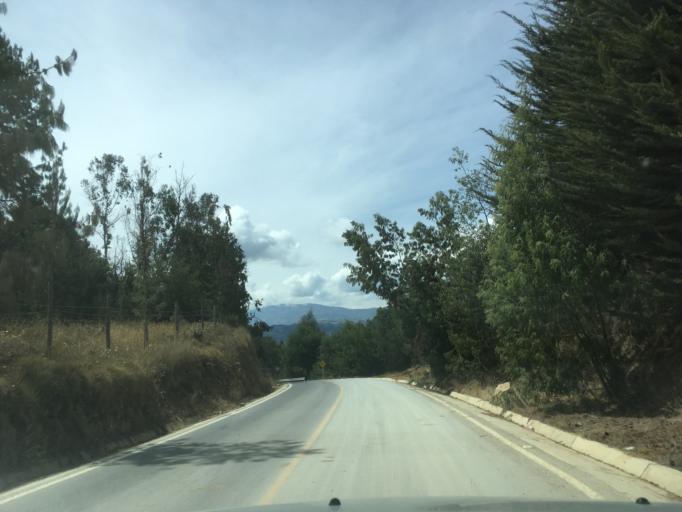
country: CO
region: Boyaca
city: Aquitania
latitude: 5.5744
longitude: -72.9454
